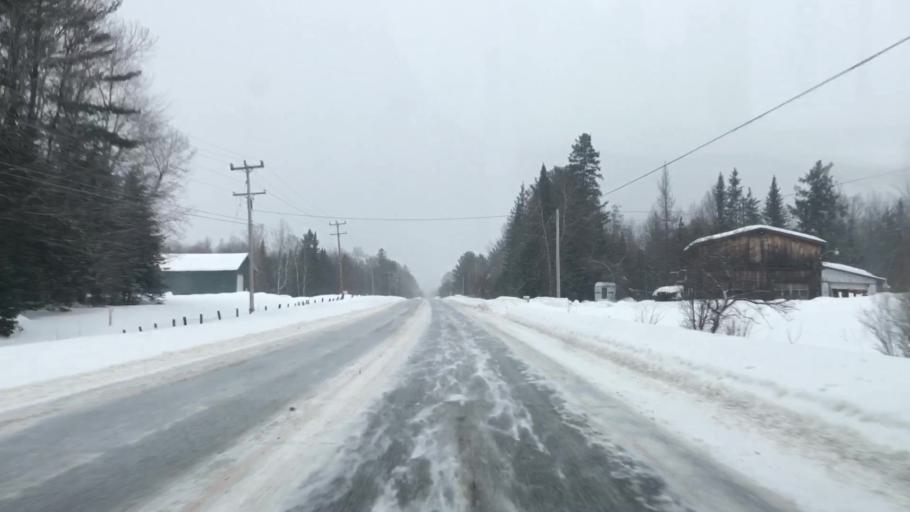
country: US
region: Maine
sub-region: Penobscot County
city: Medway
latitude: 45.5438
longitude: -68.3710
